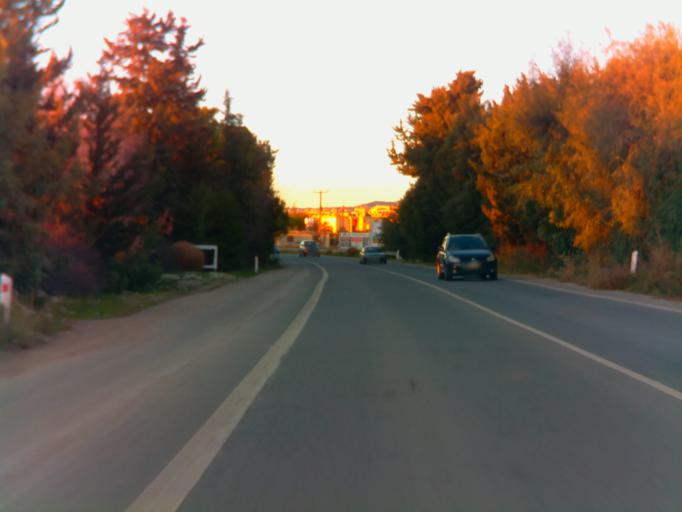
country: CY
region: Pafos
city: Chlorakas
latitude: 34.7929
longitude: 32.4018
